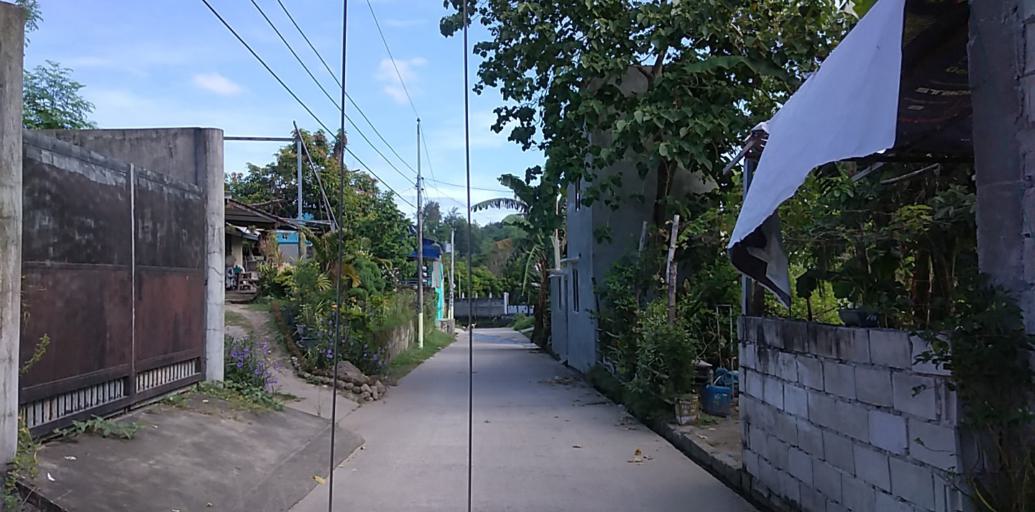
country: PH
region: Central Luzon
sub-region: Province of Pampanga
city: Porac
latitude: 15.0788
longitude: 120.5358
